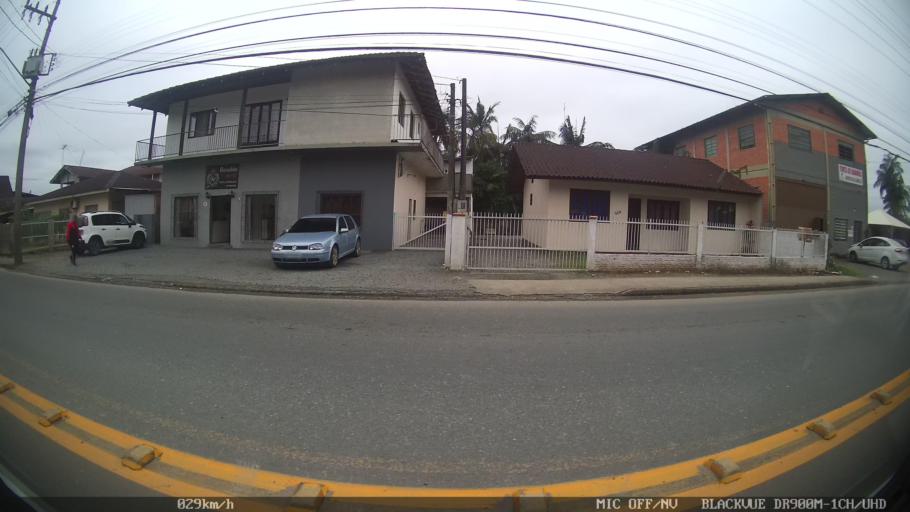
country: BR
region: Santa Catarina
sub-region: Joinville
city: Joinville
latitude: -26.2882
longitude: -48.9205
